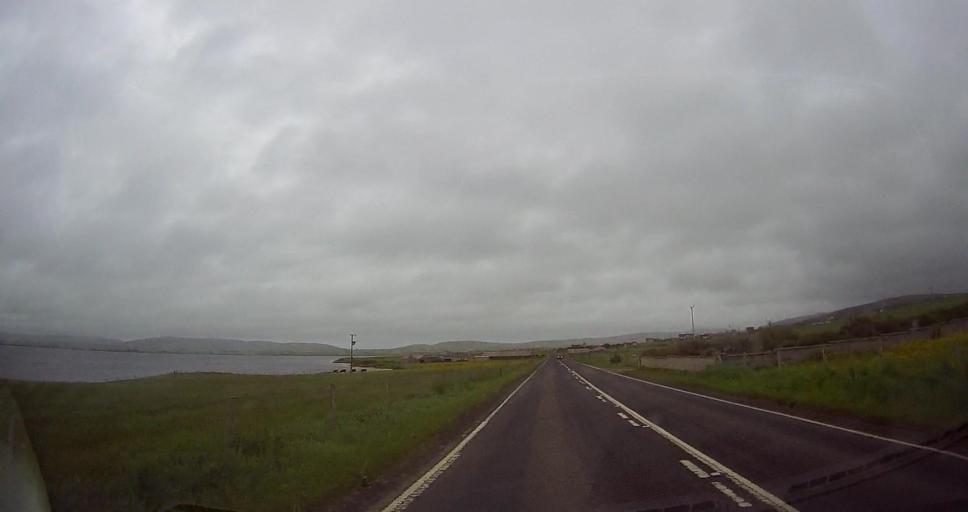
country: GB
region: Scotland
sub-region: Orkney Islands
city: Stromness
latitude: 58.9852
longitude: -3.2405
